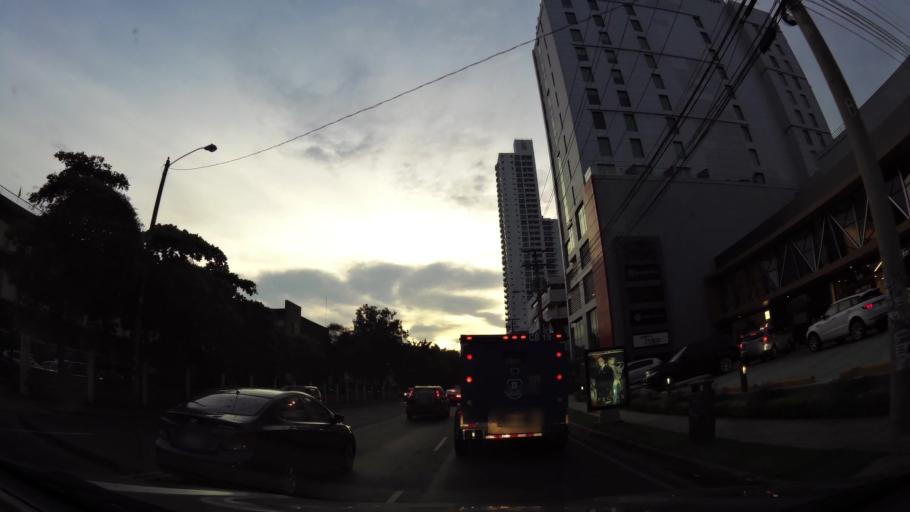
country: PA
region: Panama
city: Panama
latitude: 8.9874
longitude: -79.5068
